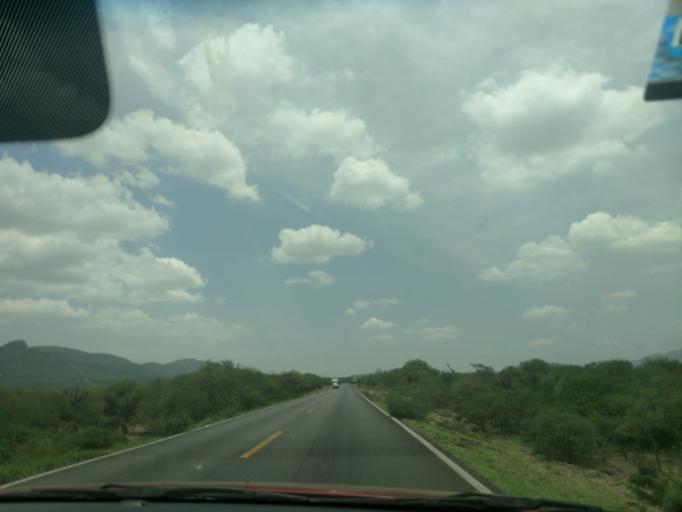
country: MX
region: San Luis Potosi
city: Villa Juarez
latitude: 22.0186
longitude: -100.3930
